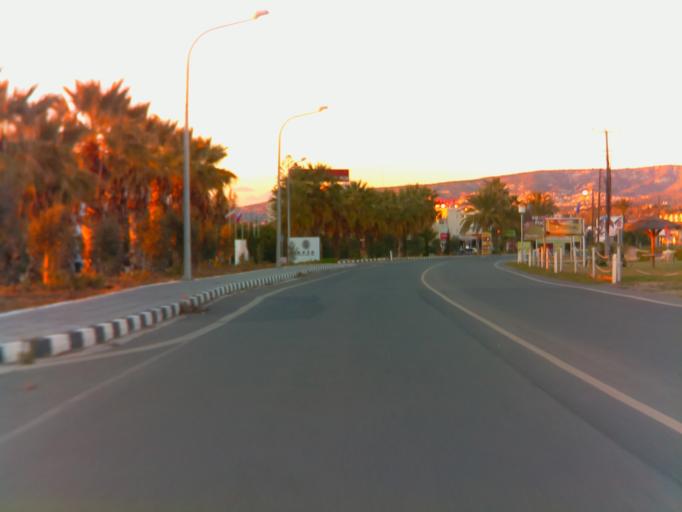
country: CY
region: Pafos
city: Kissonerga
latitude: 34.8087
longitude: 32.3964
